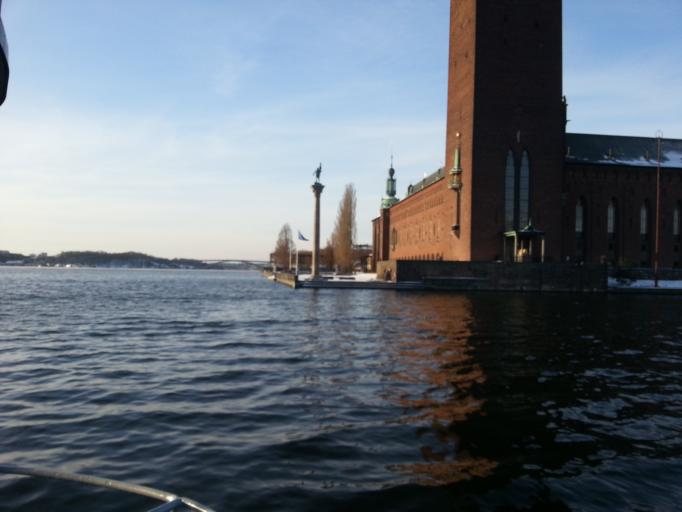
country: SE
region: Stockholm
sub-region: Stockholms Kommun
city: Stockholm
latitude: 59.3270
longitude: 18.0579
